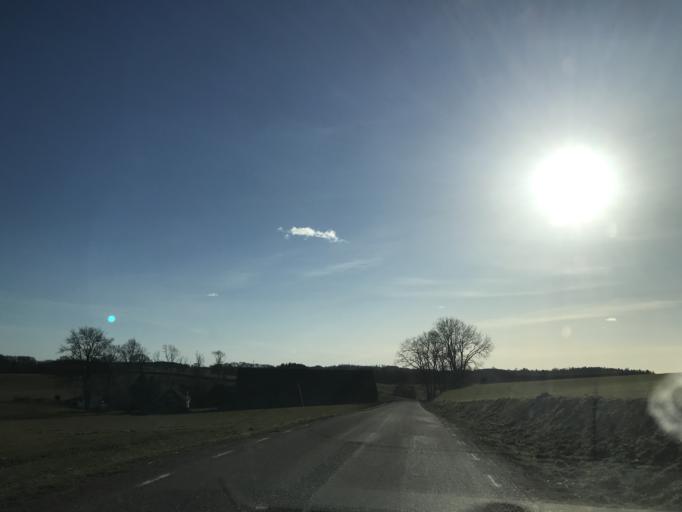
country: SE
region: Skane
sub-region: Ystads Kommun
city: Ystad
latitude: 55.5457
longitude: 13.7915
